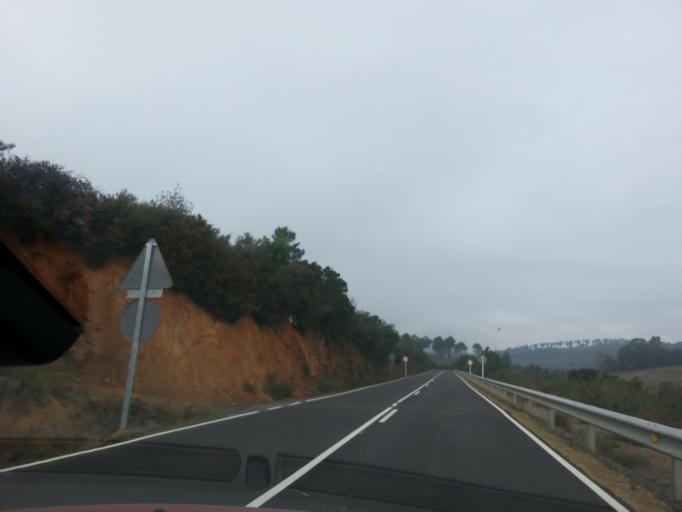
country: ES
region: Castille and Leon
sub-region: Provincia de Salamanca
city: Sotoserrano
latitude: 40.4394
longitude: -6.0455
